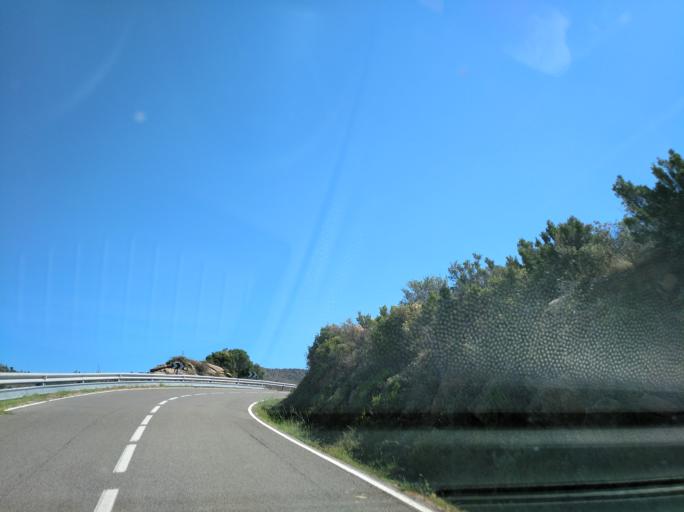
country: ES
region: Catalonia
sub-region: Provincia de Girona
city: Pau
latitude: 42.3366
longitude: 3.1278
